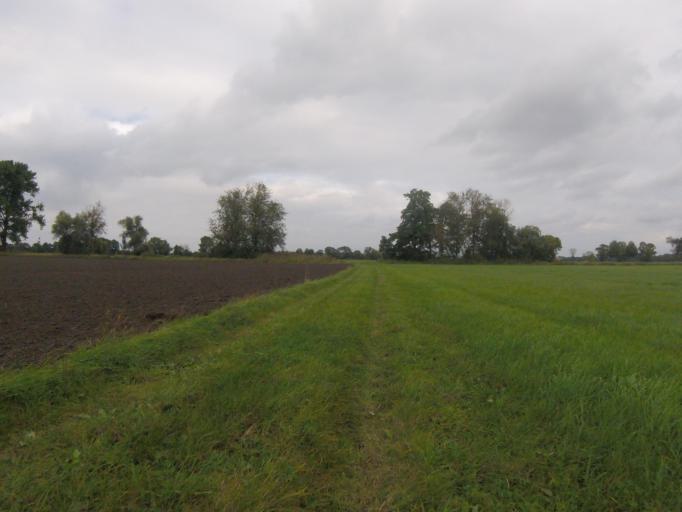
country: DE
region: Brandenburg
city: Mittenwalde
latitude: 52.2577
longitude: 13.5175
